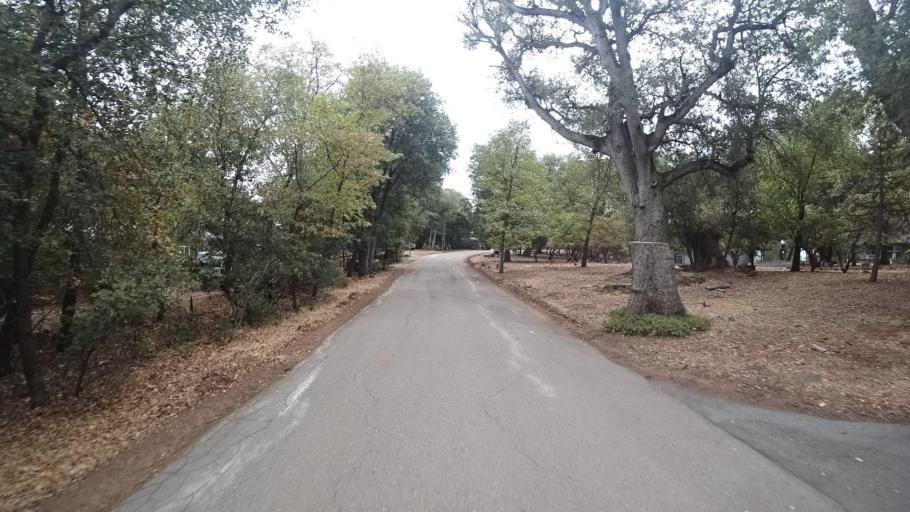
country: US
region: California
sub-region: San Diego County
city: Julian
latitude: 33.0463
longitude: -116.6269
